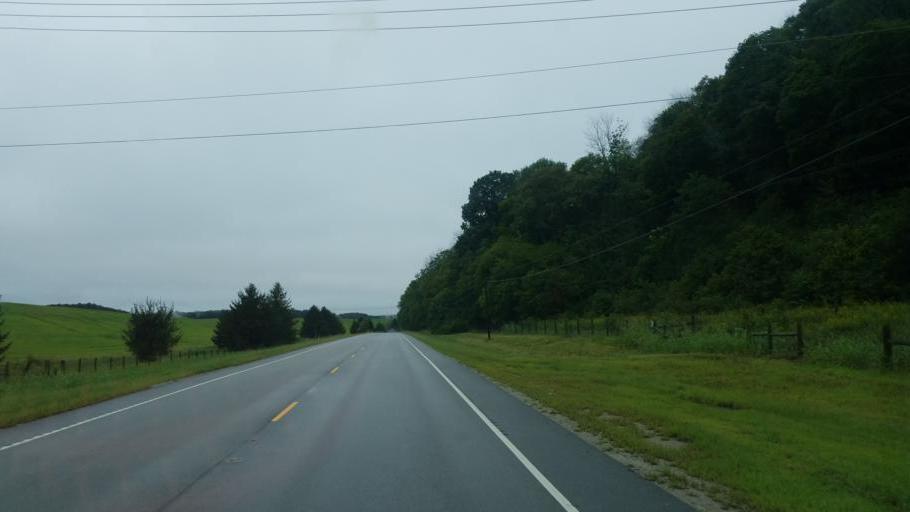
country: US
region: Ohio
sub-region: Adams County
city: Manchester
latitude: 38.6380
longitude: -83.6545
